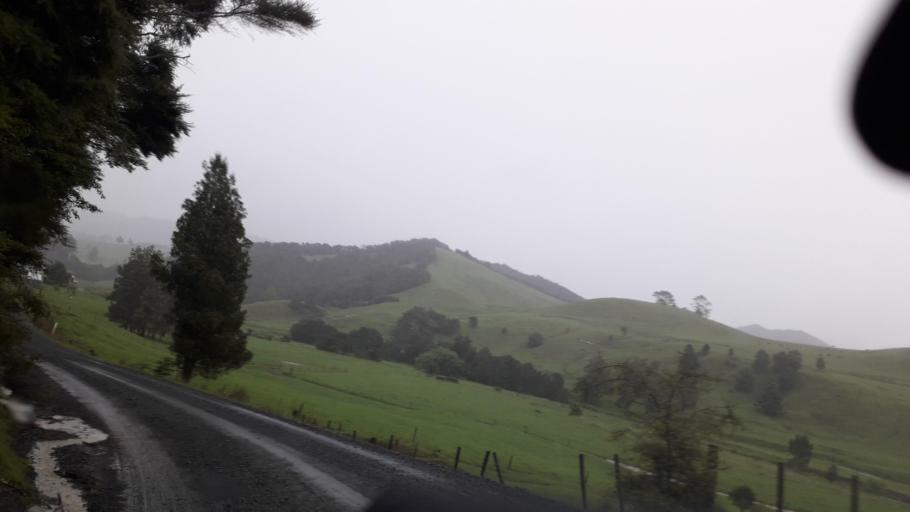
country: NZ
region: Northland
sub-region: Far North District
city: Waimate North
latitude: -35.1441
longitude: 173.7131
